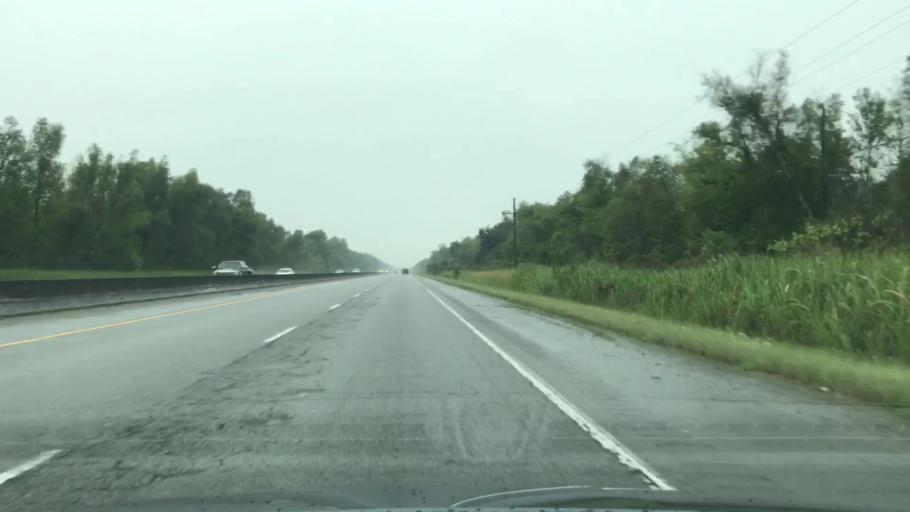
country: US
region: Louisiana
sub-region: Saint Charles Parish
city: Des Allemands
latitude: 29.7780
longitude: -90.5294
